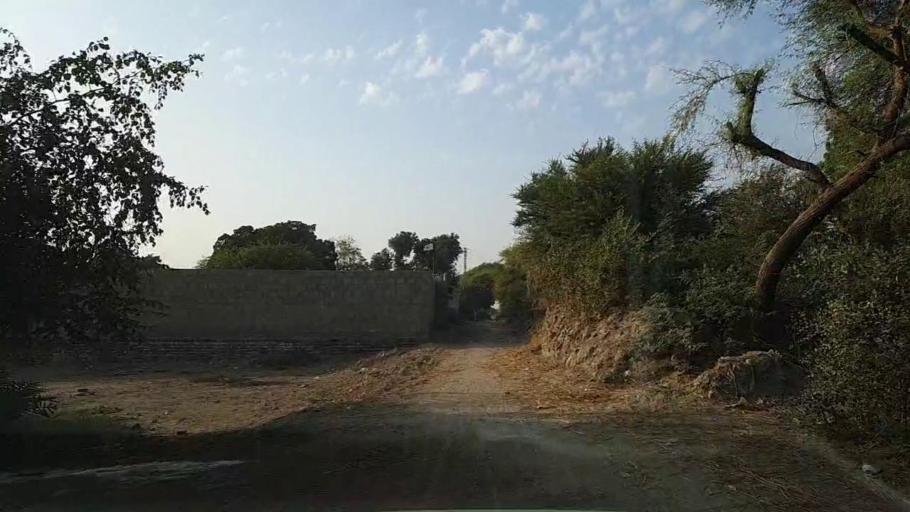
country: PK
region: Sindh
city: Daro Mehar
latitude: 24.7727
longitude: 68.1998
